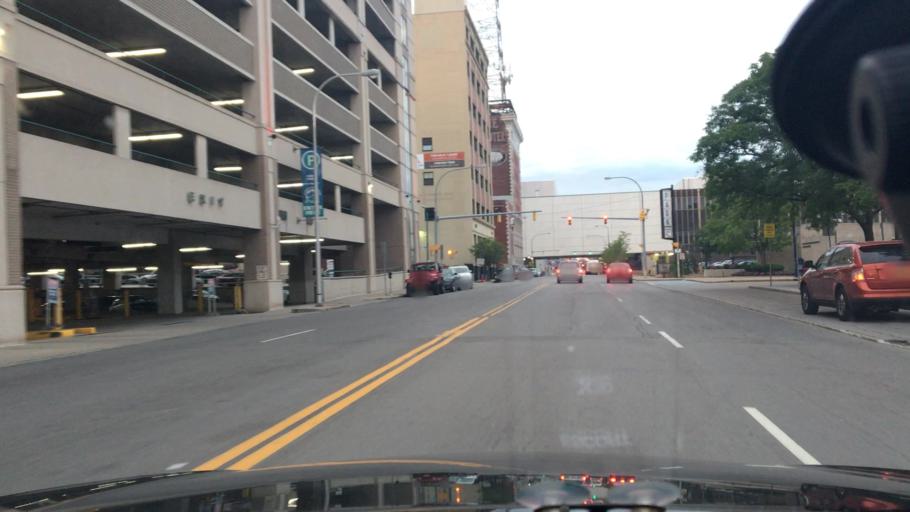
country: US
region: New York
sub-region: Erie County
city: Buffalo
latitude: 42.8832
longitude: -78.8728
